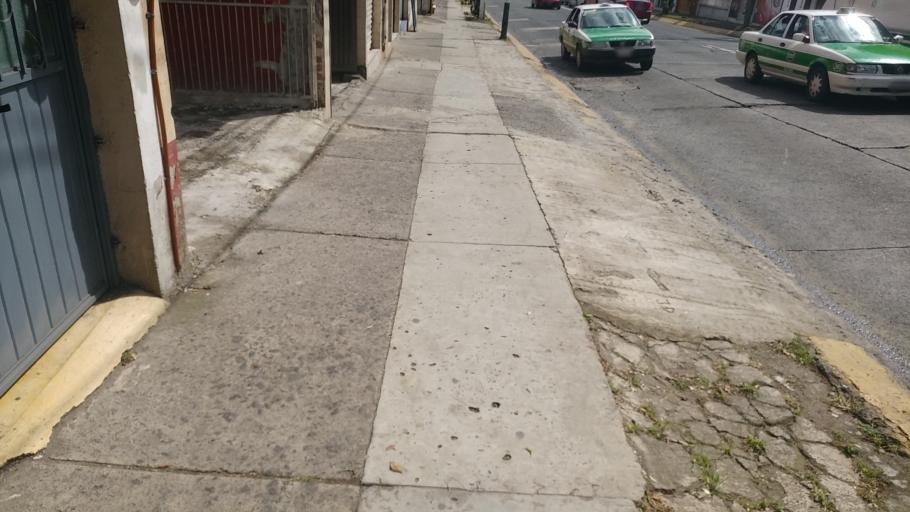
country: MX
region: Veracruz
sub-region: Xalapa
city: Xalapa de Enriquez
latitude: 19.5285
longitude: -96.9121
